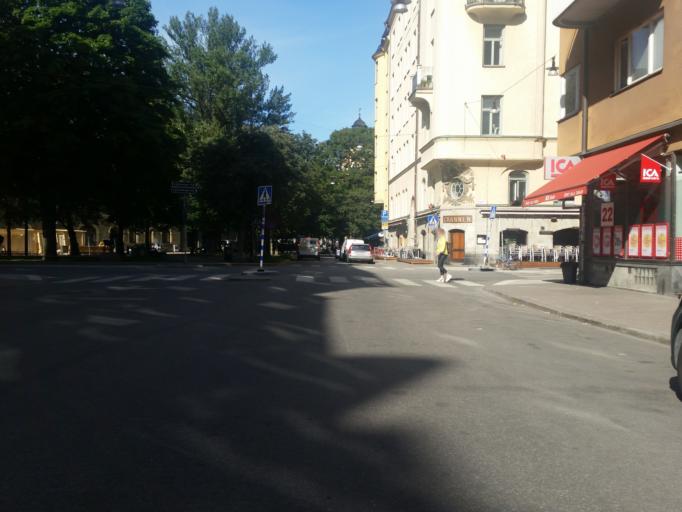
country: SE
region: Stockholm
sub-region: Stockholms Kommun
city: Stockholm
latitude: 59.3121
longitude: 18.0782
